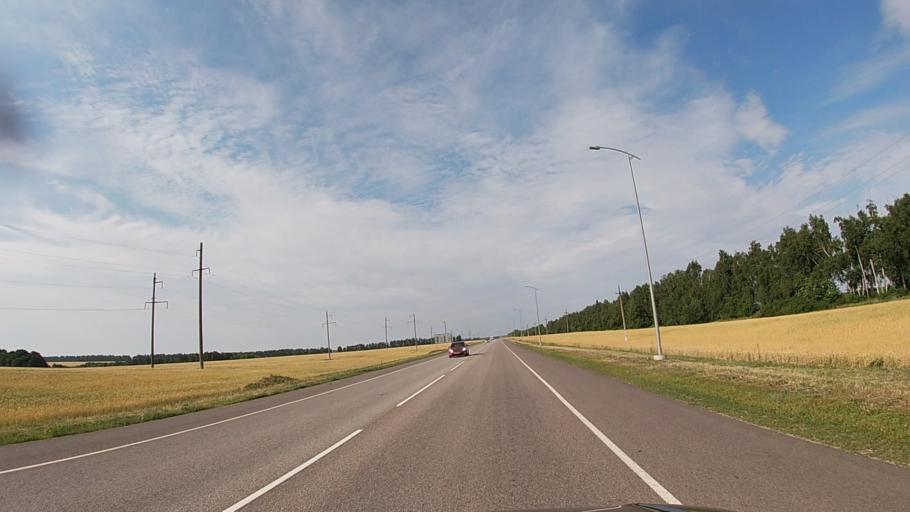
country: RU
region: Belgorod
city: Proletarskiy
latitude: 50.8296
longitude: 35.7646
